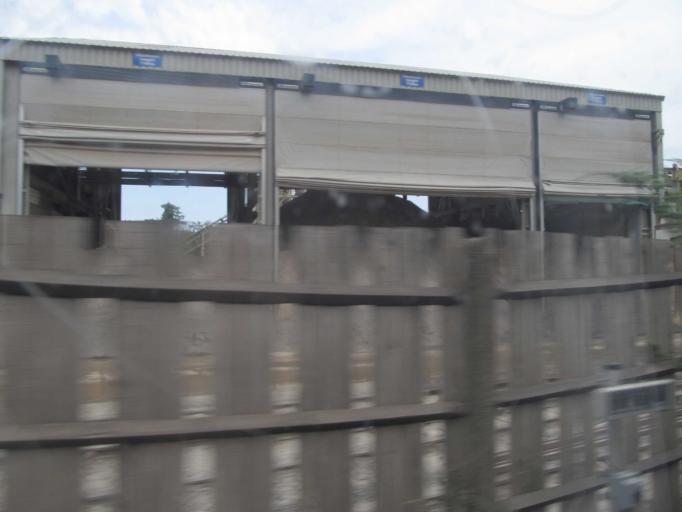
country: GB
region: England
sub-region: Greater London
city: West Drayton
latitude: 51.5075
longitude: -0.4488
